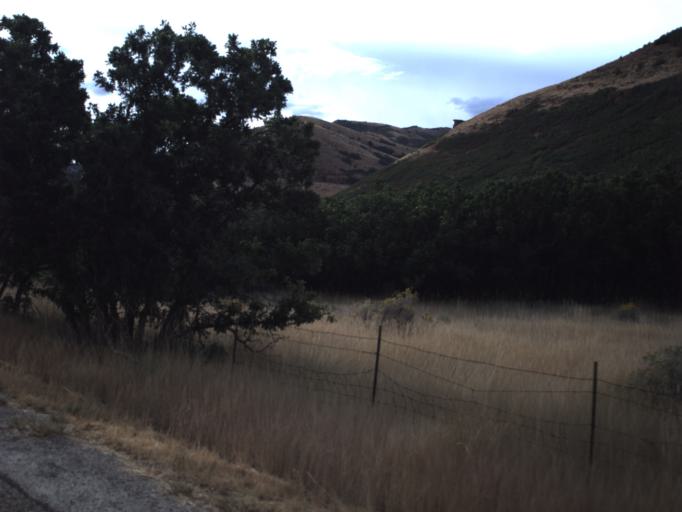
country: US
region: Utah
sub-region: Morgan County
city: Morgan
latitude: 40.9455
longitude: -111.6521
